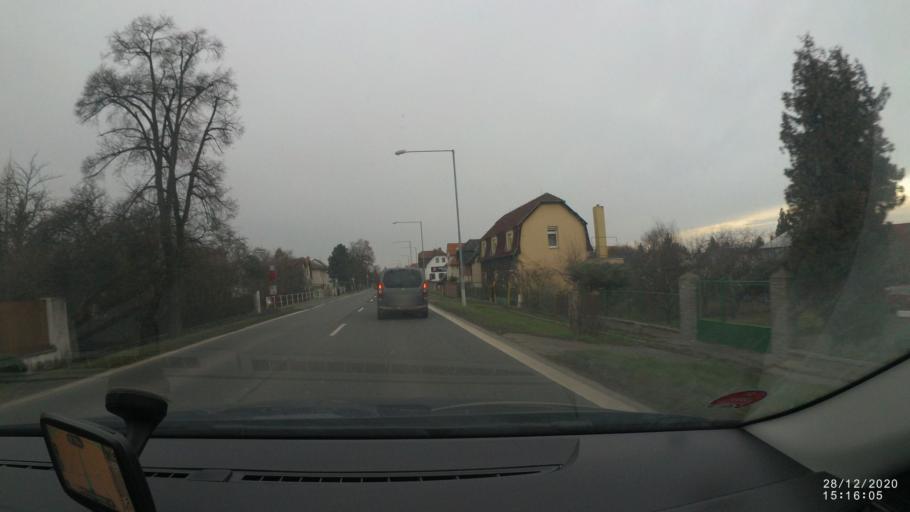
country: CZ
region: Central Bohemia
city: Sestajovice
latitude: 50.0731
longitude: 14.6791
